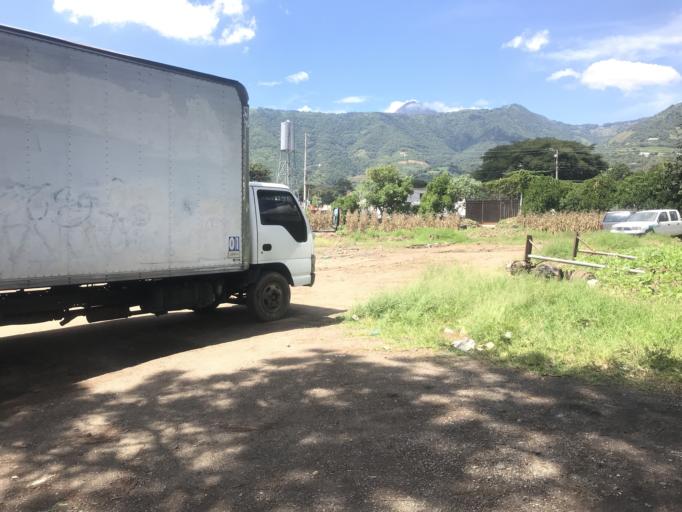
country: GT
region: Guatemala
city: Amatitlan
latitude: 14.4801
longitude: -90.6324
